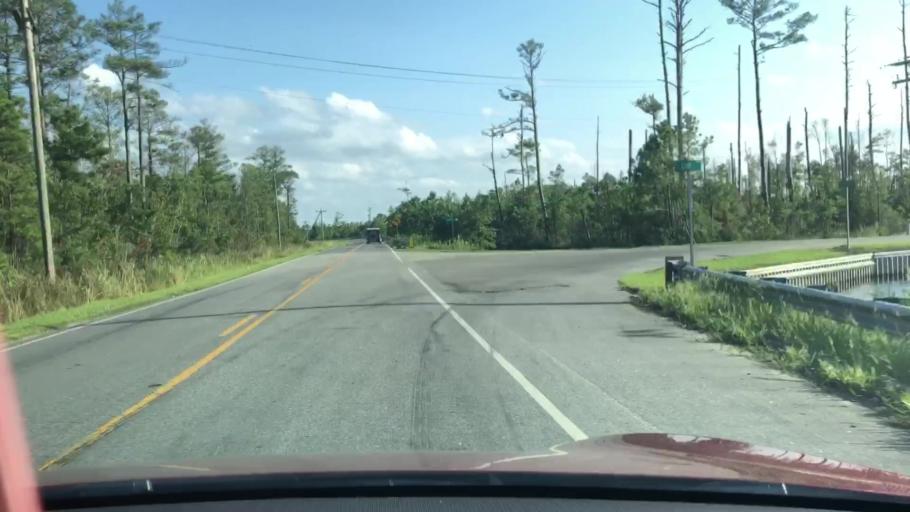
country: US
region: North Carolina
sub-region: Dare County
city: Manteo
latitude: 35.8344
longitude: -75.8107
